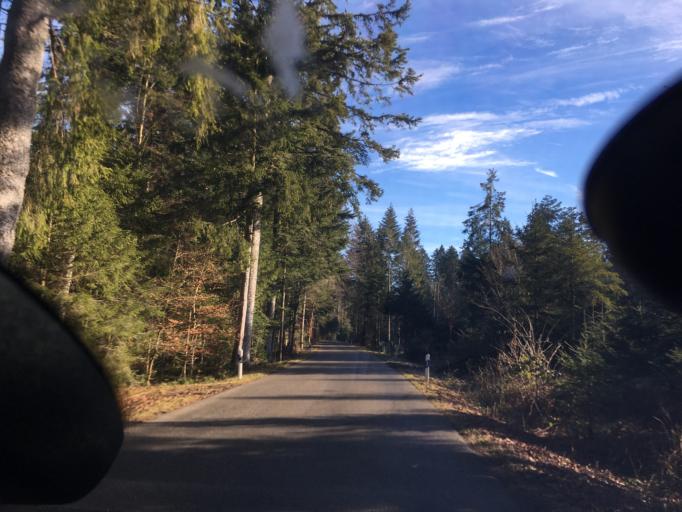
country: DE
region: Baden-Wuerttemberg
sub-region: Freiburg Region
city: Gorwihl
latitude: 47.6519
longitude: 8.0457
